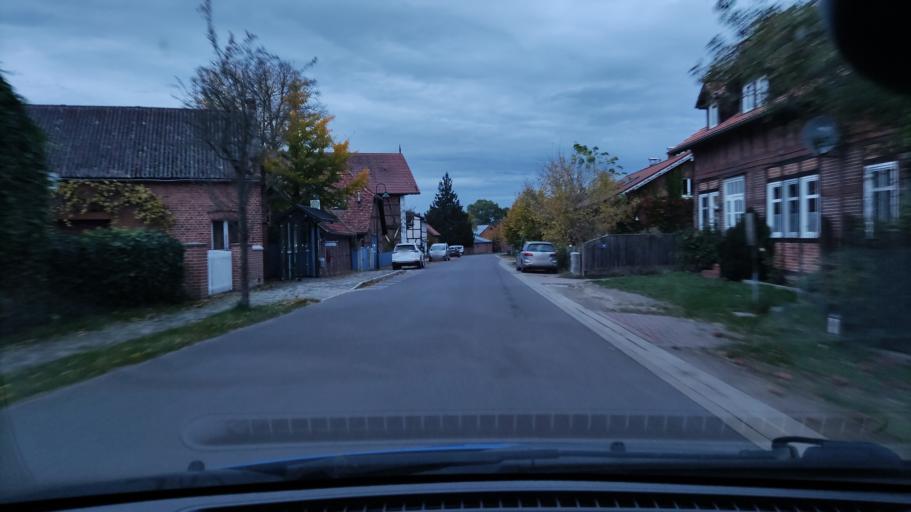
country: DE
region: Lower Saxony
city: Gorleben
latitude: 53.0685
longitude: 11.4056
